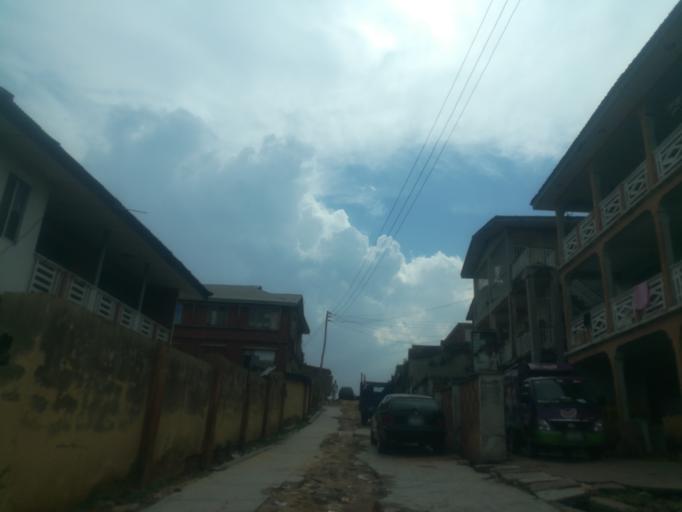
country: NG
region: Oyo
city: Ibadan
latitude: 7.4125
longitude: 3.8926
